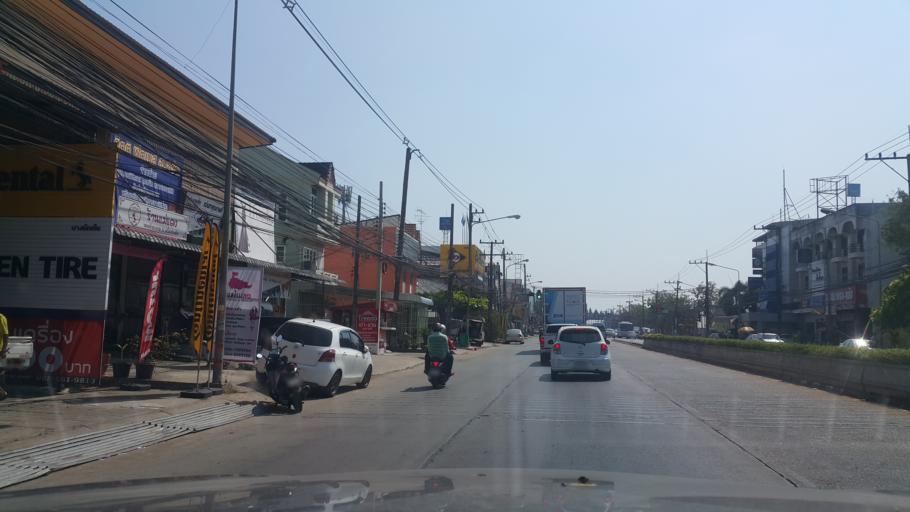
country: TH
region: Changwat Udon Thani
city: Udon Thani
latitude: 17.3885
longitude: 102.8015
